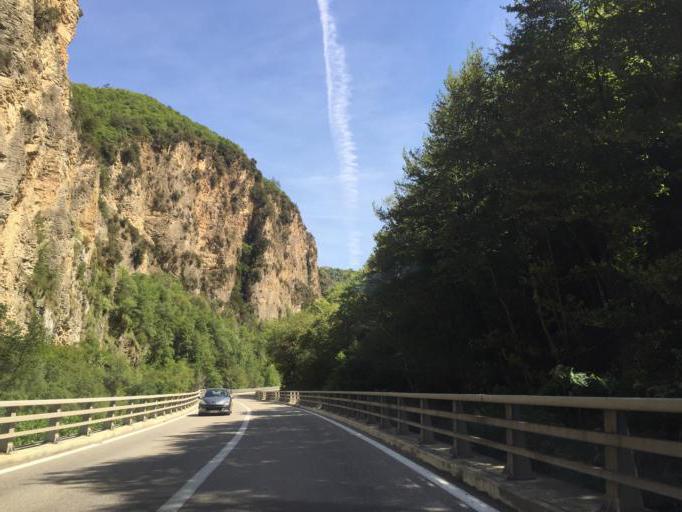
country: FR
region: Provence-Alpes-Cote d'Azur
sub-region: Departement des Alpes-Maritimes
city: Saint-Martin-Vesubie
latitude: 44.0077
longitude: 7.1345
